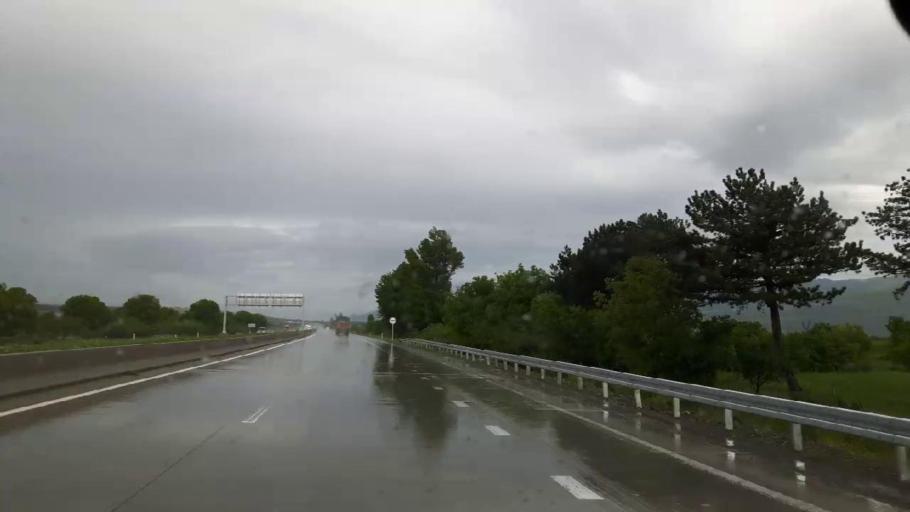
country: GE
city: Agara
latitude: 42.0303
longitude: 43.9533
